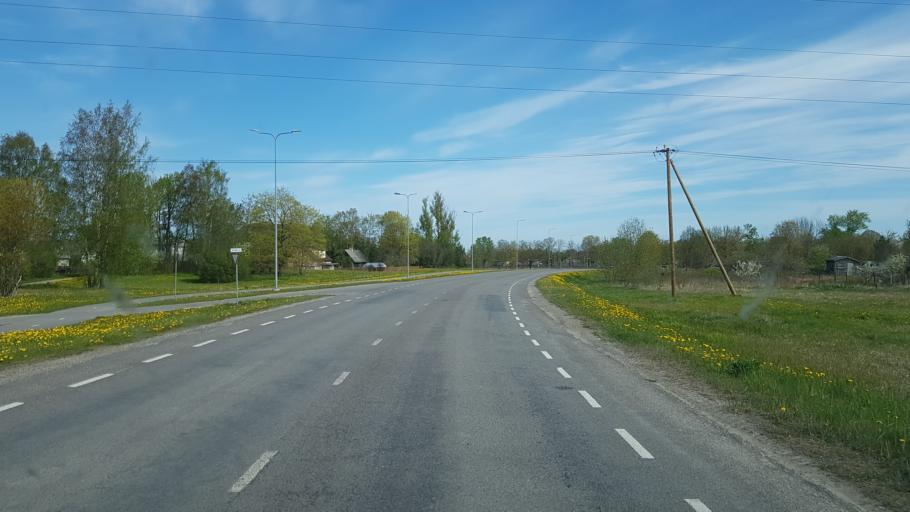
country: EE
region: Ida-Virumaa
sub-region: Kivioli linn
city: Kivioli
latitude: 59.3500
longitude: 26.9674
